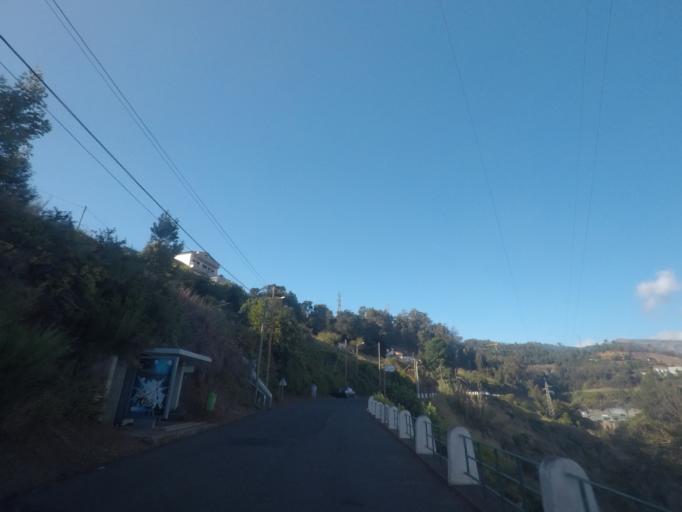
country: PT
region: Madeira
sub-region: Ribeira Brava
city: Campanario
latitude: 32.6637
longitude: -17.0029
